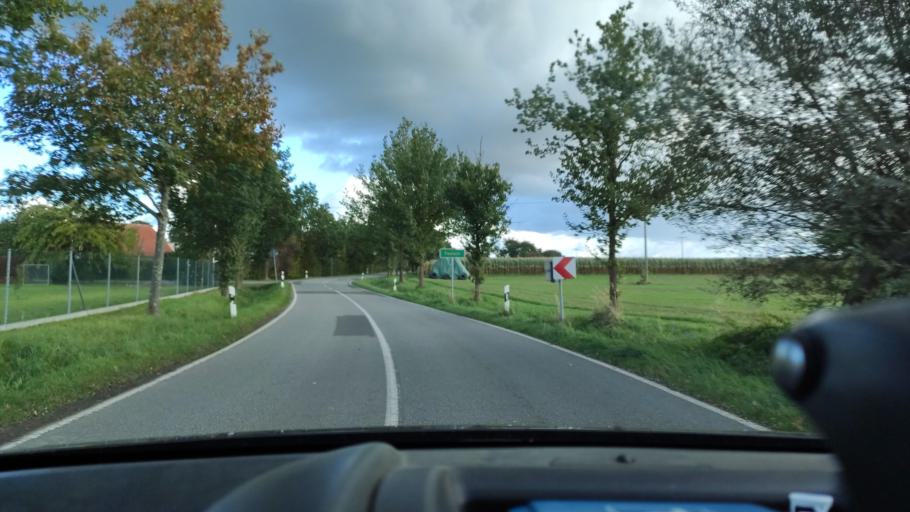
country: DE
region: Mecklenburg-Vorpommern
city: Butzow
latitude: 53.8018
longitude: 11.9581
